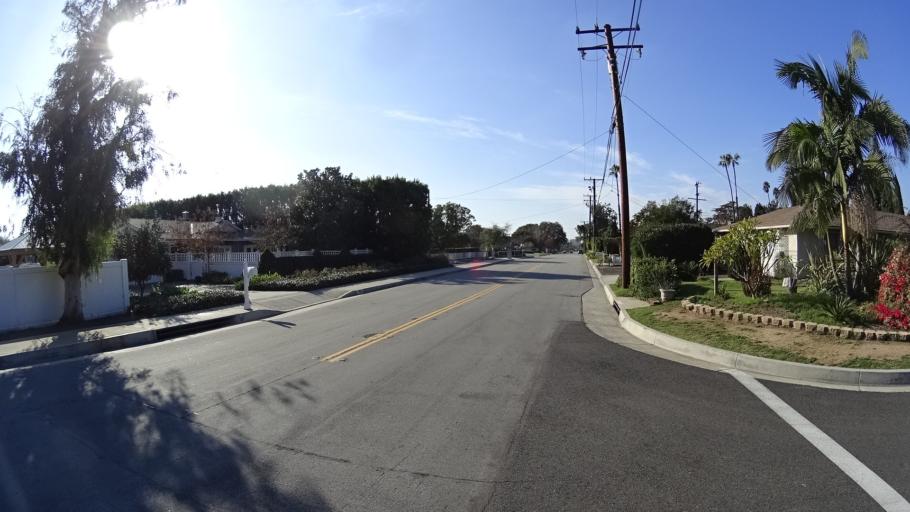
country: US
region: California
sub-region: Orange County
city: North Tustin
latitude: 33.7567
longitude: -117.8081
